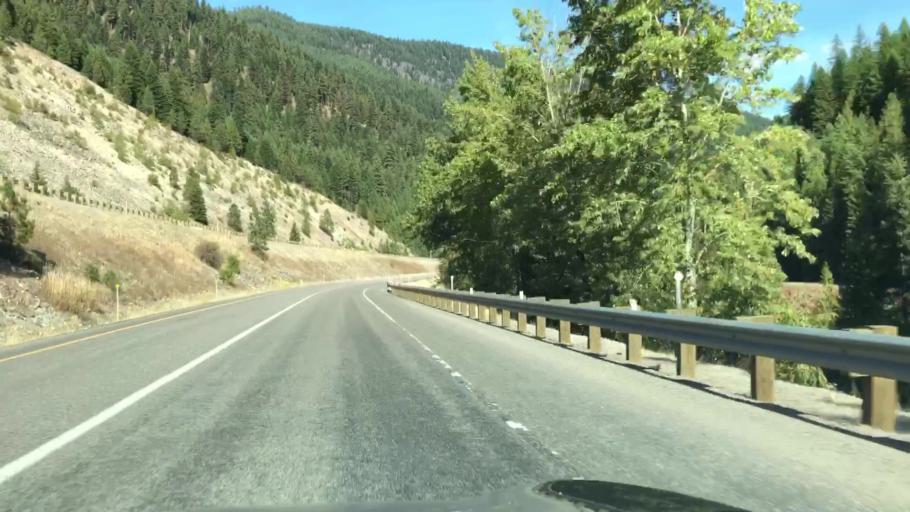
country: US
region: Montana
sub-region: Sanders County
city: Thompson Falls
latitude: 47.3129
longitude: -115.2311
